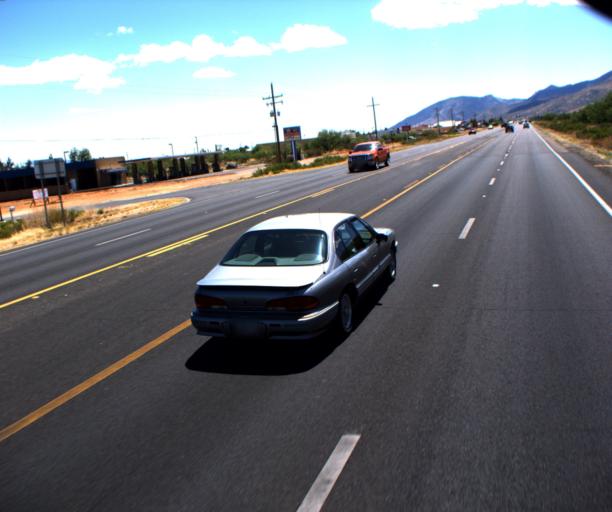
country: US
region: Arizona
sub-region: Cochise County
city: Sierra Vista Southeast
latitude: 31.4951
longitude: -110.2575
